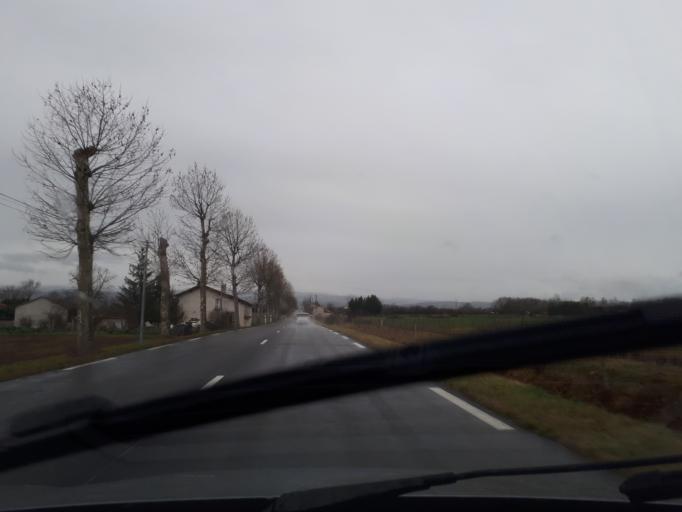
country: FR
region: Rhone-Alpes
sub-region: Departement de la Loire
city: Boen-sur-Lignon
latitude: 45.7381
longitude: 4.1140
